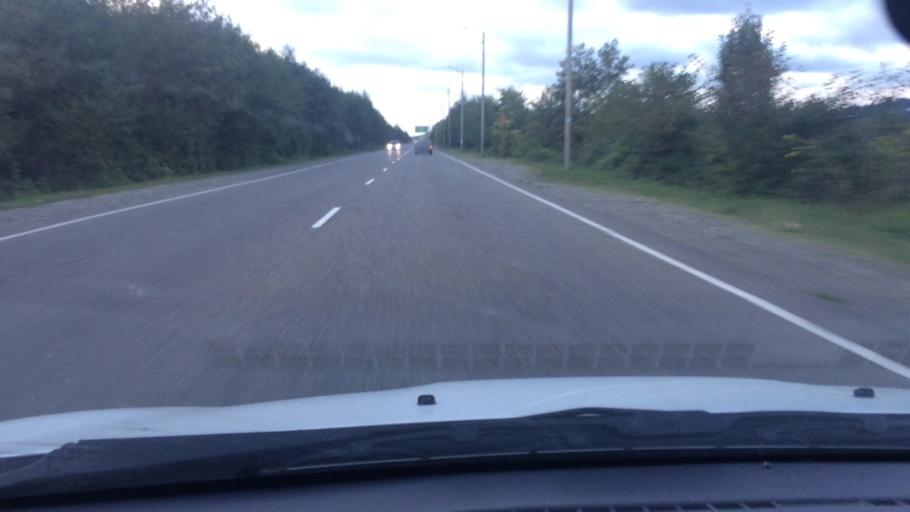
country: GE
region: Guria
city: Urek'i
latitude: 41.9302
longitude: 41.7726
